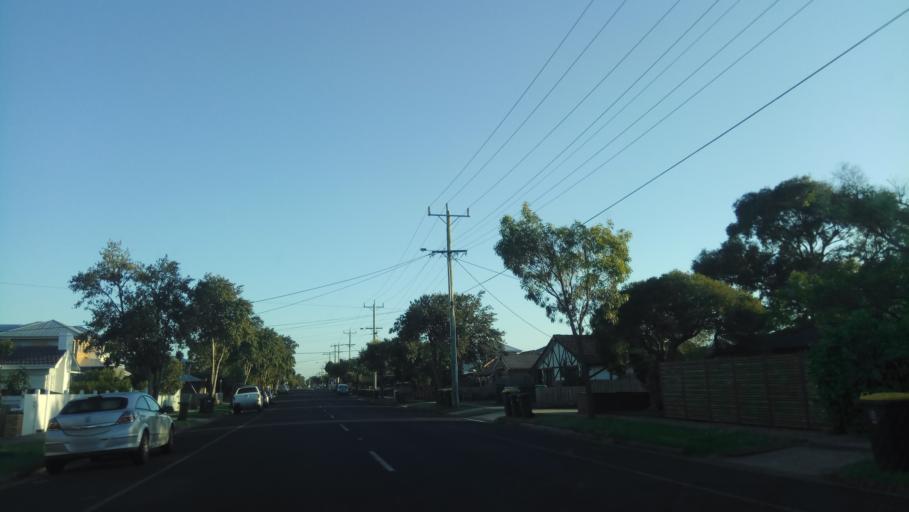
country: AU
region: Victoria
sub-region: Hobsons Bay
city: Altona
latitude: -37.8680
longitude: 144.8178
